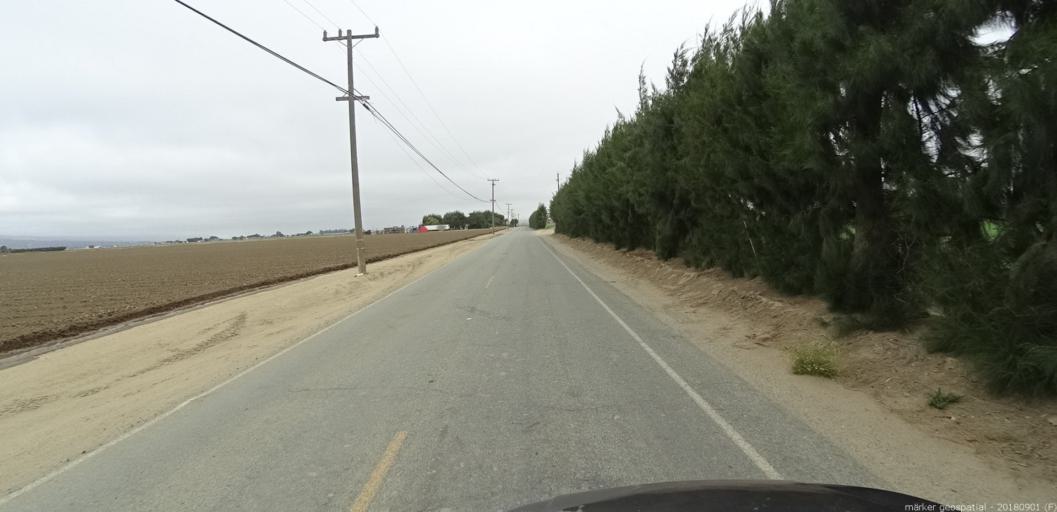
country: US
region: California
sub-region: Monterey County
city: Soledad
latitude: 36.3896
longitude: -121.3325
